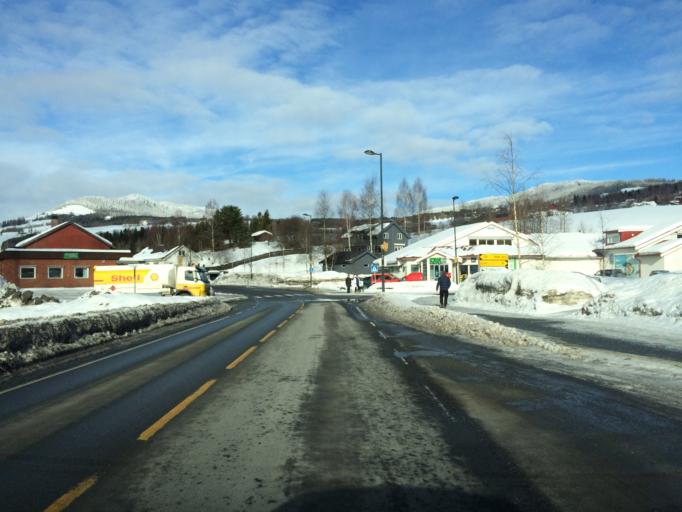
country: NO
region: Oppland
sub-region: Gausdal
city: Segalstad bru
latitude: 61.2154
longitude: 10.2855
